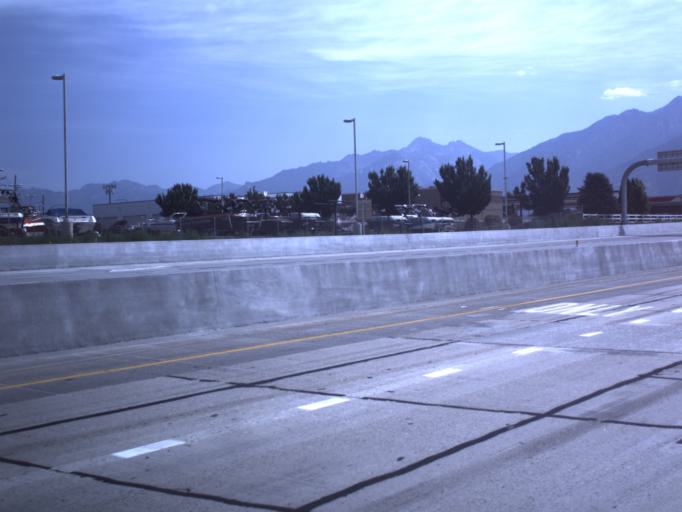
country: US
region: Utah
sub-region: Salt Lake County
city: Draper
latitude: 40.5042
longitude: -111.8991
